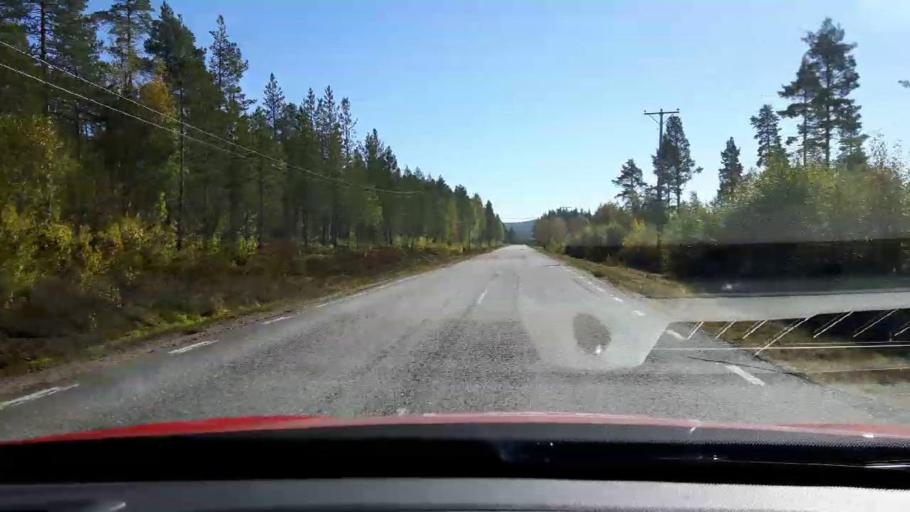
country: SE
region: Jaemtland
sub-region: Harjedalens Kommun
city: Sveg
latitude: 62.3003
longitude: 14.0653
